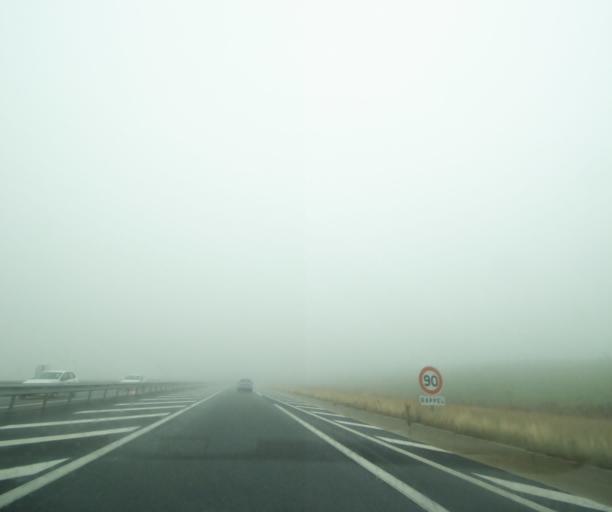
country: FR
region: Midi-Pyrenees
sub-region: Departement de l'Aveyron
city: Baraqueville
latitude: 44.2240
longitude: 2.4075
